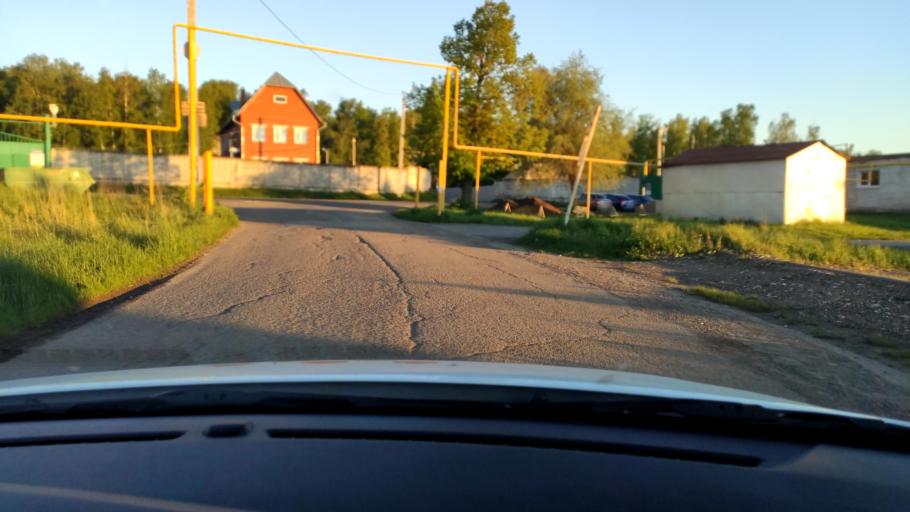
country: RU
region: Tatarstan
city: Vysokaya Gora
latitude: 55.9293
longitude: 49.3108
